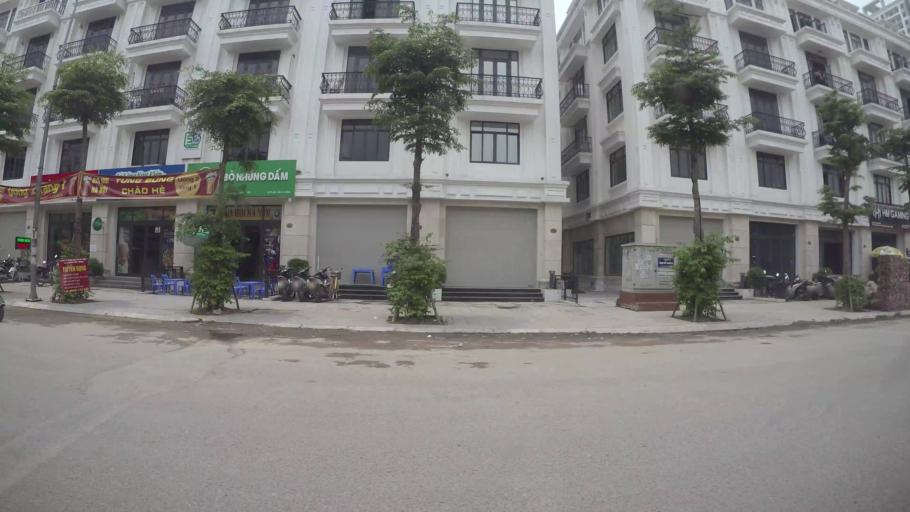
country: VN
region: Ha Noi
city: Tay Ho
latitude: 21.0675
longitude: 105.8038
